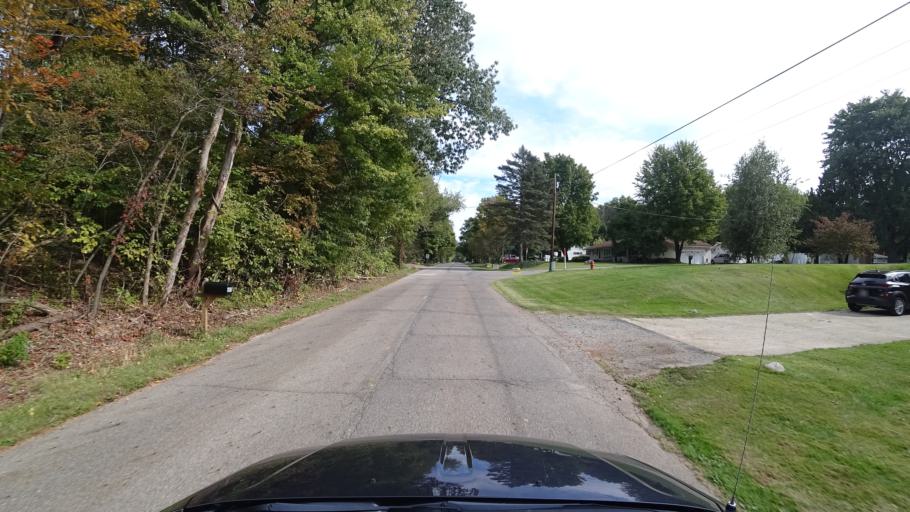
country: US
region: Indiana
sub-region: LaPorte County
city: Trail Creek
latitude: 41.7092
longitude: -86.8355
